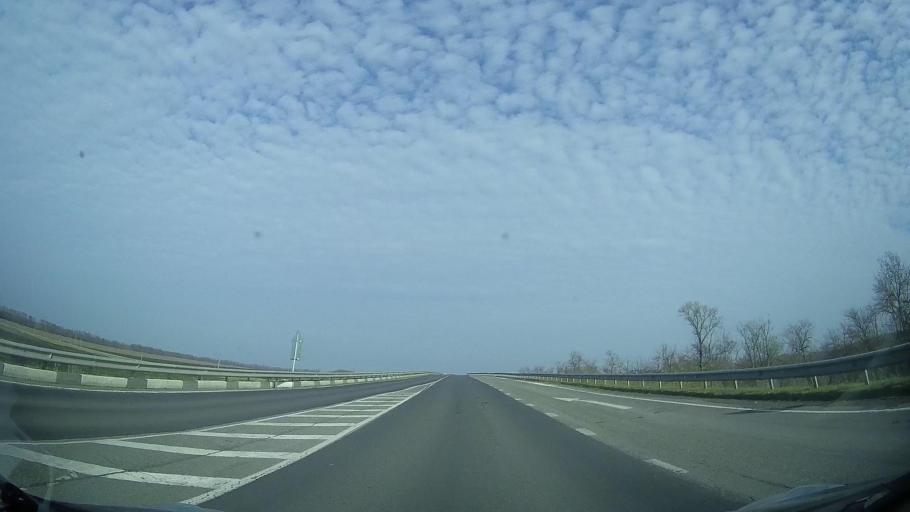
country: RU
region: Rostov
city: Tselina
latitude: 46.5265
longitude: 41.1670
